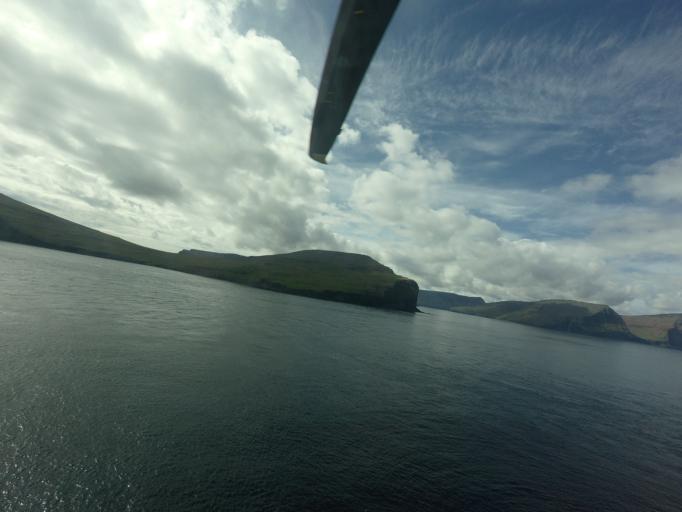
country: FO
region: Nordoyar
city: Klaksvik
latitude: 62.3167
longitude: -6.3128
